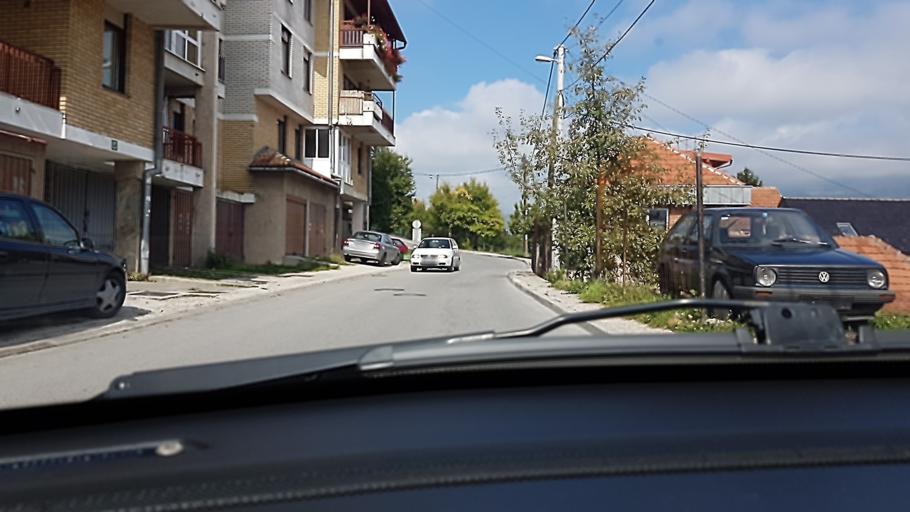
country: BA
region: Federation of Bosnia and Herzegovina
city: Kobilja Glava
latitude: 43.8616
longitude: 18.4086
